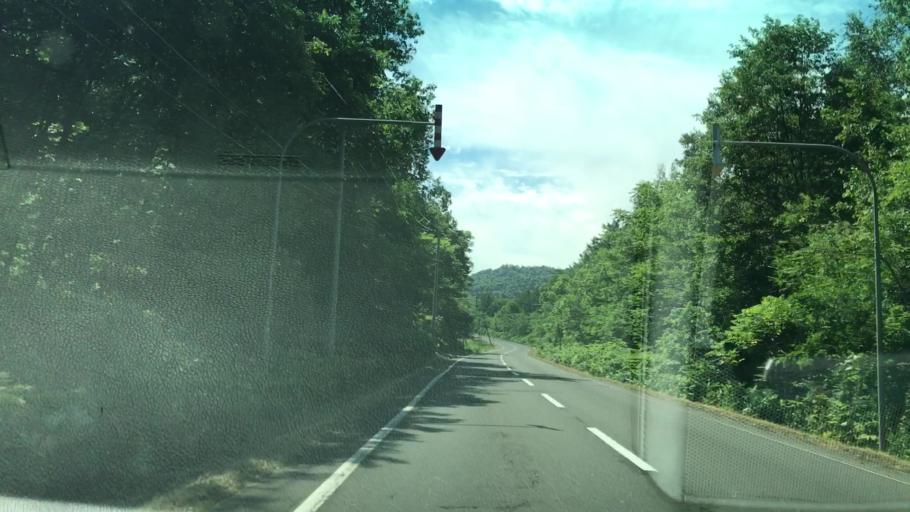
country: JP
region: Hokkaido
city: Shimo-furano
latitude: 42.9614
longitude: 142.4283
